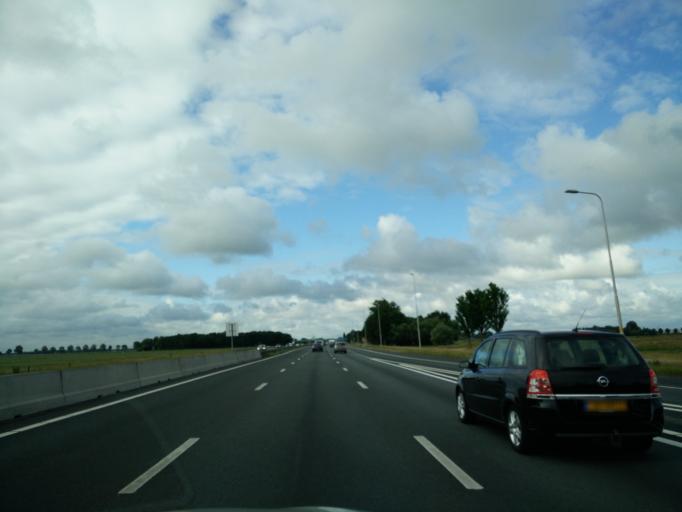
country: NL
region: Overijssel
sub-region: Gemeente Staphorst
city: Staphorst
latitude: 52.5799
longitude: 6.1909
